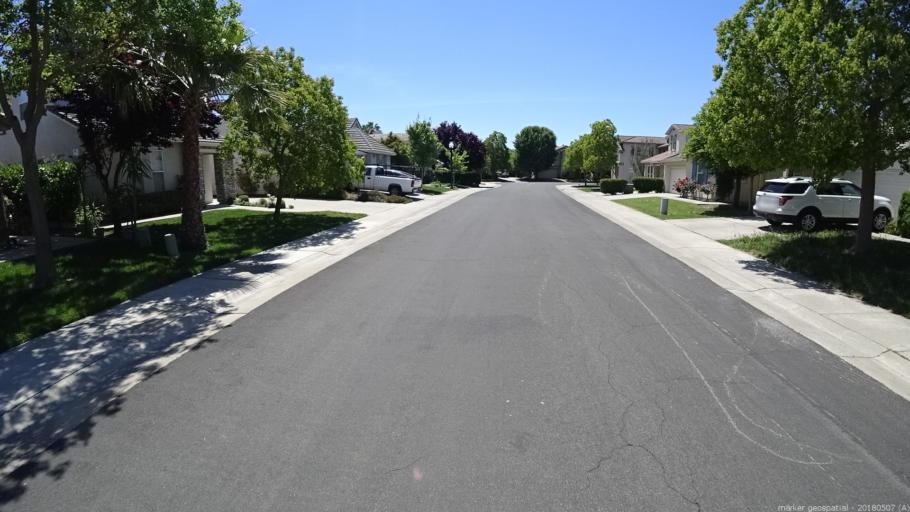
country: US
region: California
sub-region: Sacramento County
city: Elverta
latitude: 38.6755
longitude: -121.5152
